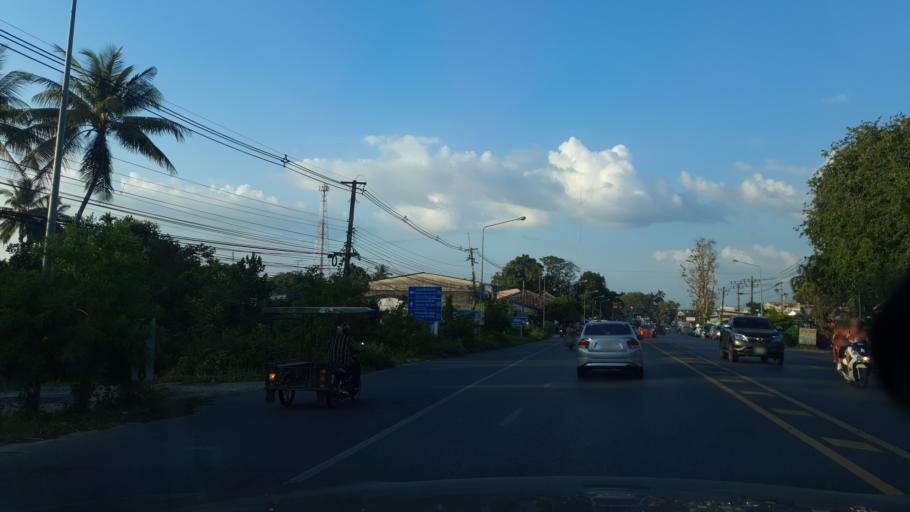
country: TH
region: Phangnga
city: Takua Pa
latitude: 8.8375
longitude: 98.2836
